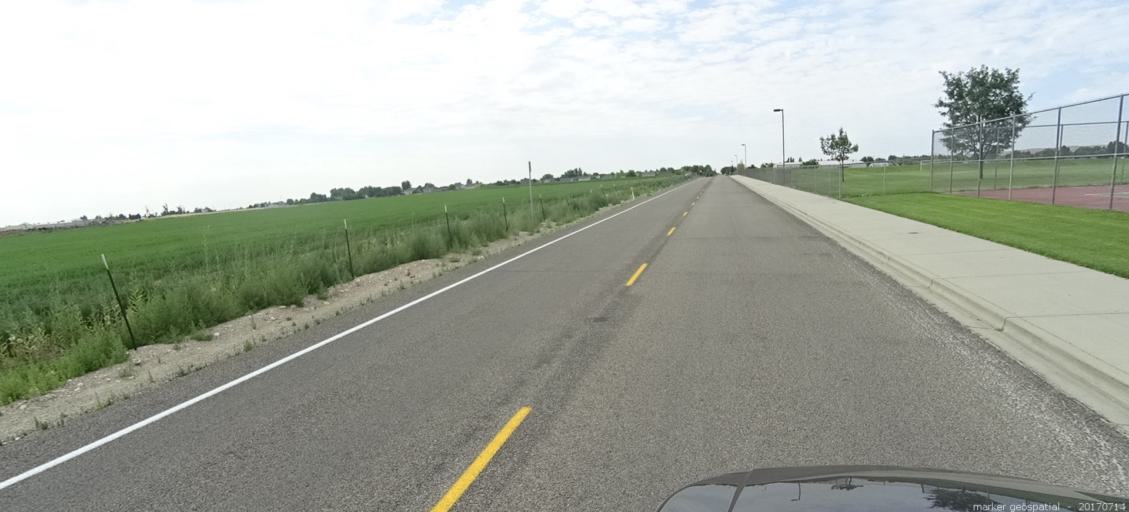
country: US
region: Idaho
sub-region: Ada County
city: Kuna
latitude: 43.5007
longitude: -116.4039
